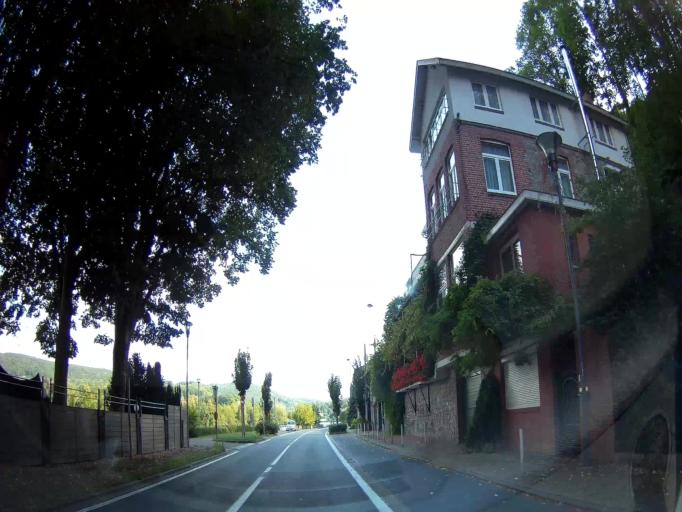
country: BE
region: Wallonia
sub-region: Province de Namur
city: Yvoir
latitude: 50.3452
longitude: 4.8542
